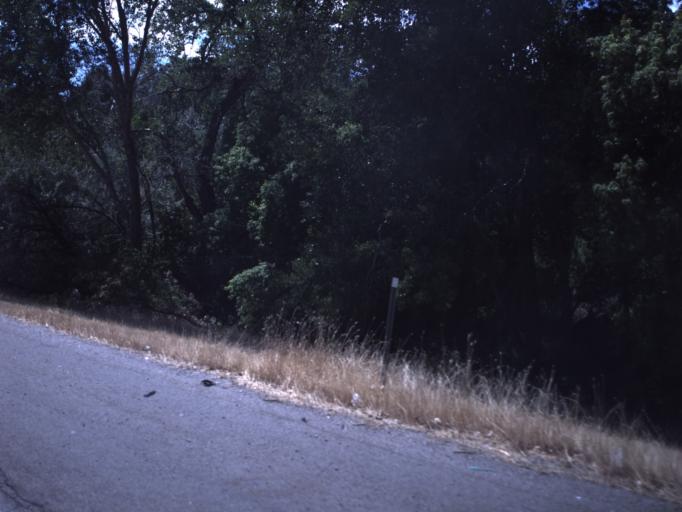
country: US
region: Utah
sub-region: Weber County
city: Riverdale
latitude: 41.1612
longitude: -111.9954
